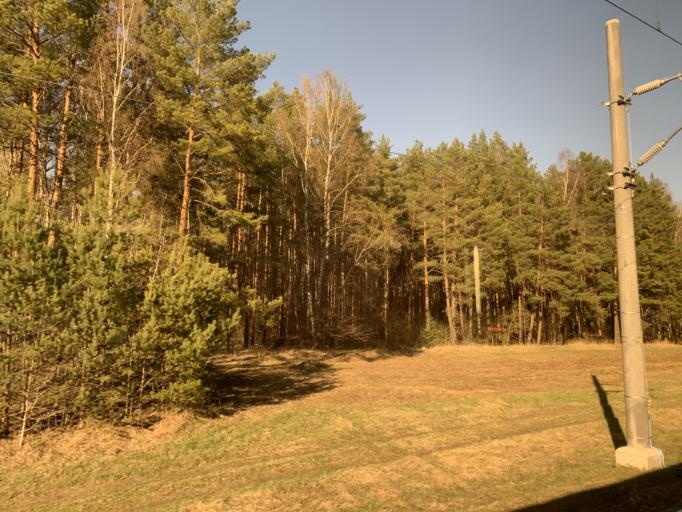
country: BY
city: Soly
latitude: 54.4920
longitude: 26.2894
